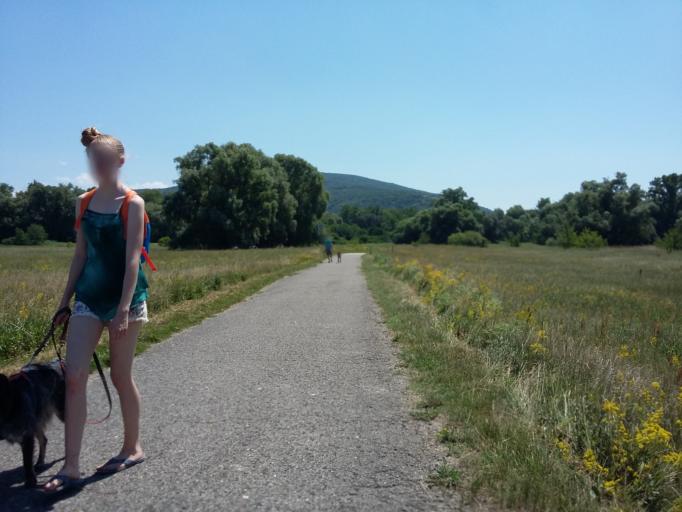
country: AT
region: Lower Austria
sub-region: Politischer Bezirk Bruck an der Leitha
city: Hainburg an der Donau
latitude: 48.2139
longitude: 16.9658
